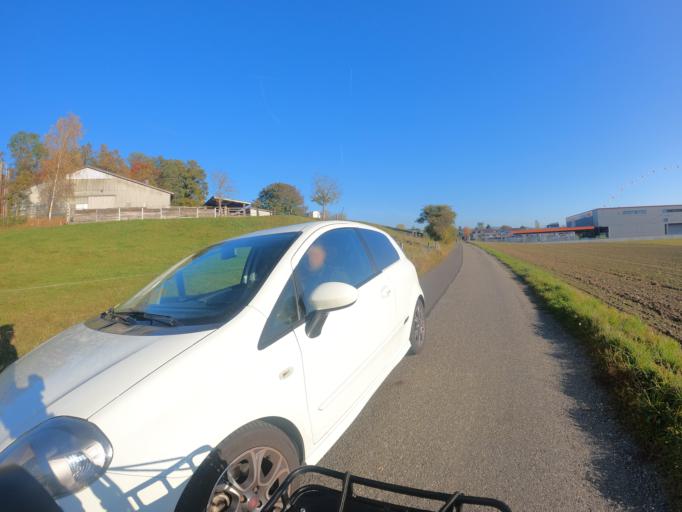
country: CH
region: Zurich
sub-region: Bezirk Affoltern
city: Affoltern / Oberdorf
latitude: 47.2779
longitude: 8.4371
